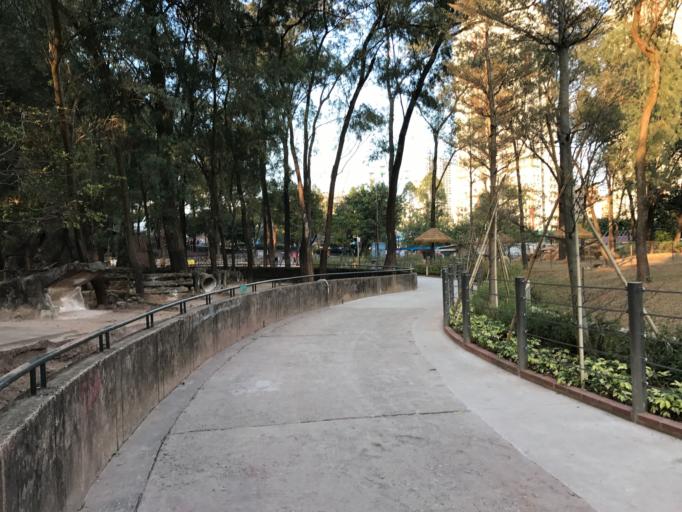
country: CN
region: Guangdong
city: Wushan
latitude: 23.1408
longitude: 113.3013
